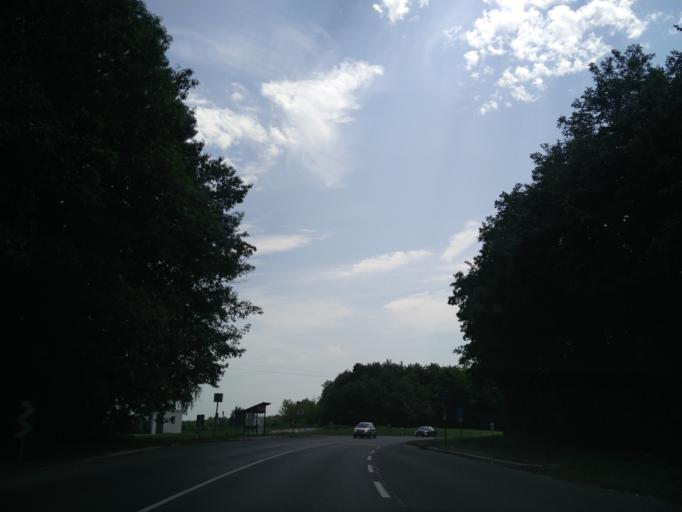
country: HU
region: Zala
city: Zalaegerszeg
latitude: 46.8769
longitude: 16.8533
